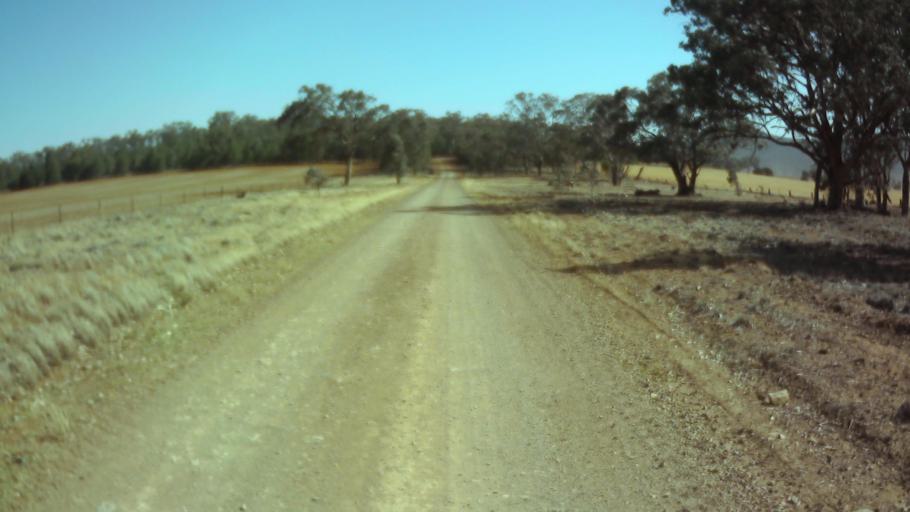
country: AU
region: New South Wales
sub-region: Weddin
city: Grenfell
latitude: -33.8585
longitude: 148.0154
